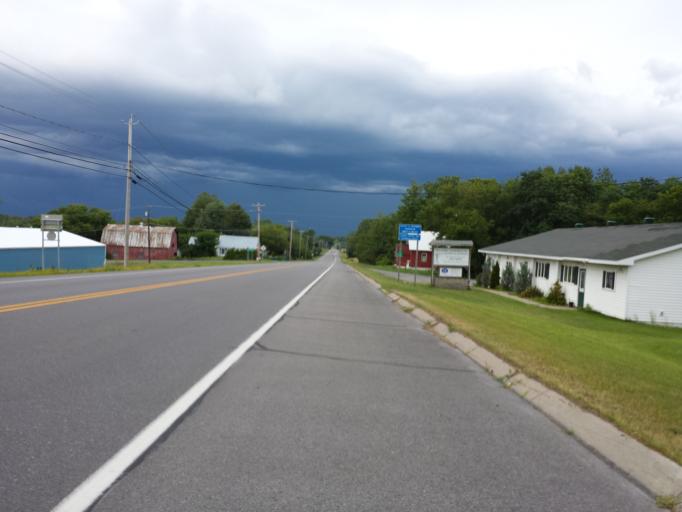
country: US
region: New York
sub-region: St. Lawrence County
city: Norwood
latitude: 44.7133
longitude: -74.9872
